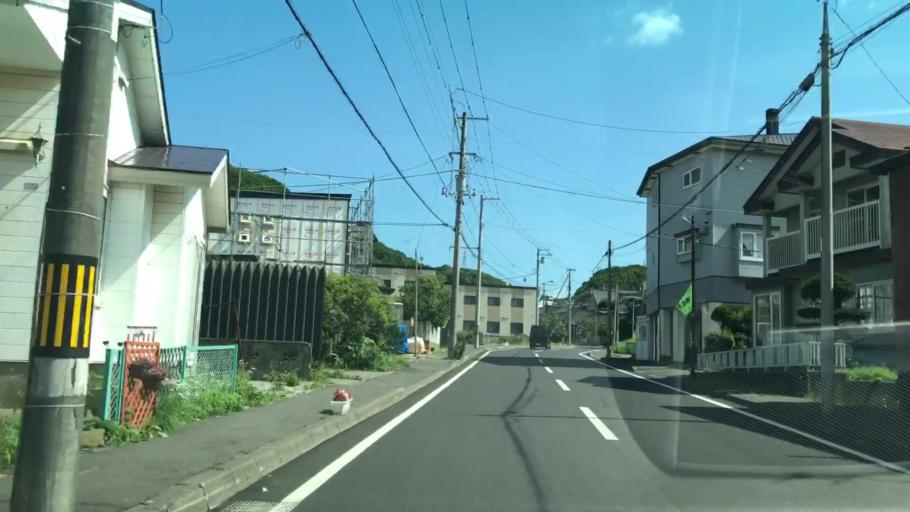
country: JP
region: Hokkaido
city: Muroran
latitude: 42.3099
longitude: 140.9976
